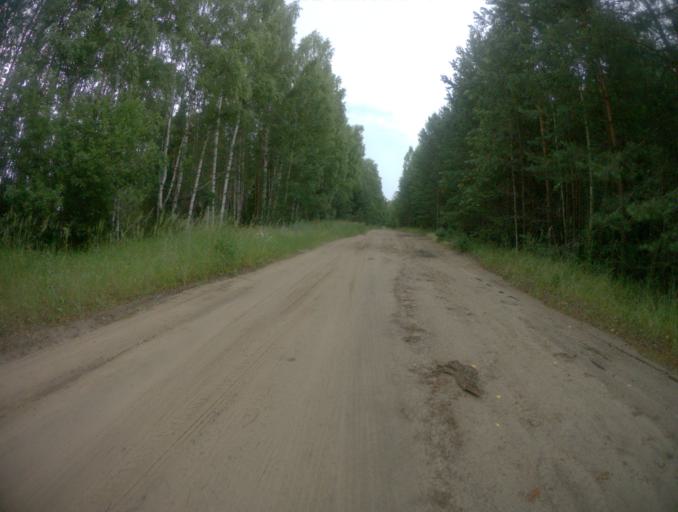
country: RU
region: Ivanovo
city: Talitsy
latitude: 56.6044
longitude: 42.4346
